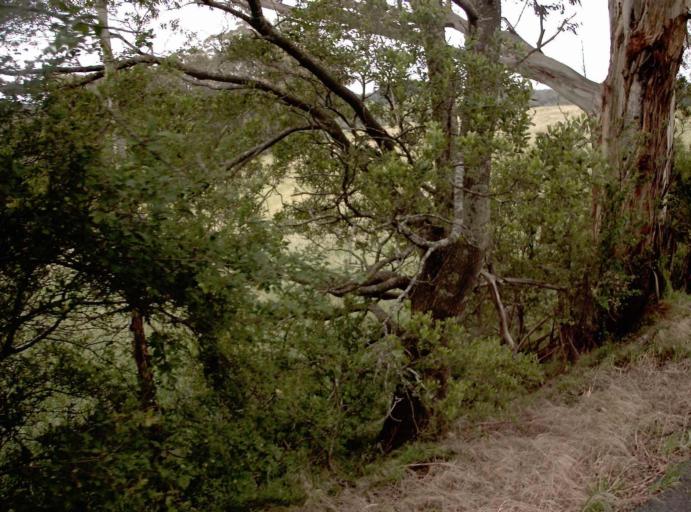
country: AU
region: Victoria
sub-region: Latrobe
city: Moe
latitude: -37.9500
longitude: 146.1208
